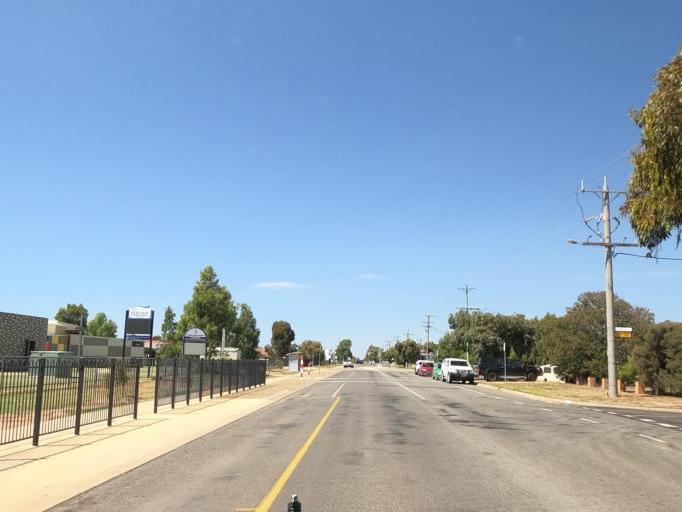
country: AU
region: Victoria
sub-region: Moira
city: Yarrawonga
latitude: -36.0119
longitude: 146.0132
